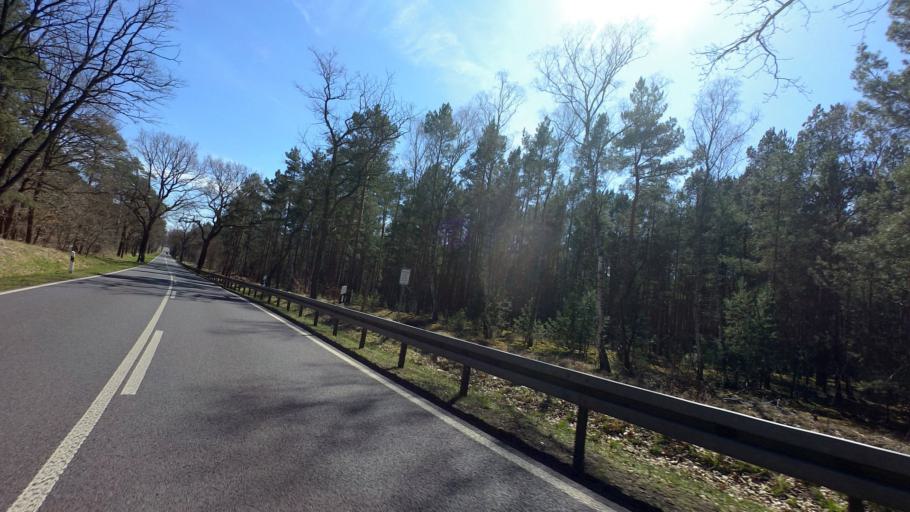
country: DE
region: Brandenburg
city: Storkow
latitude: 52.2277
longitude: 13.9680
